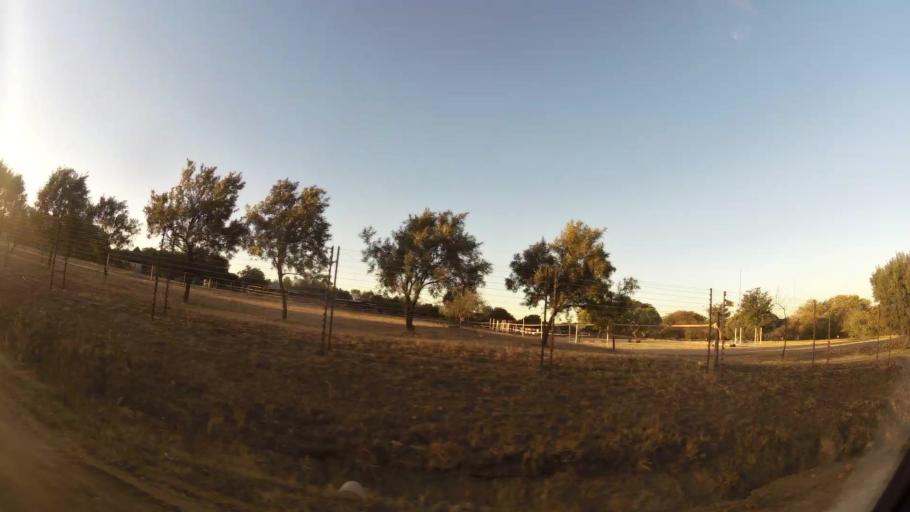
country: ZA
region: Gauteng
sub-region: City of Johannesburg Metropolitan Municipality
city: Diepsloot
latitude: -25.9403
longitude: 28.0524
